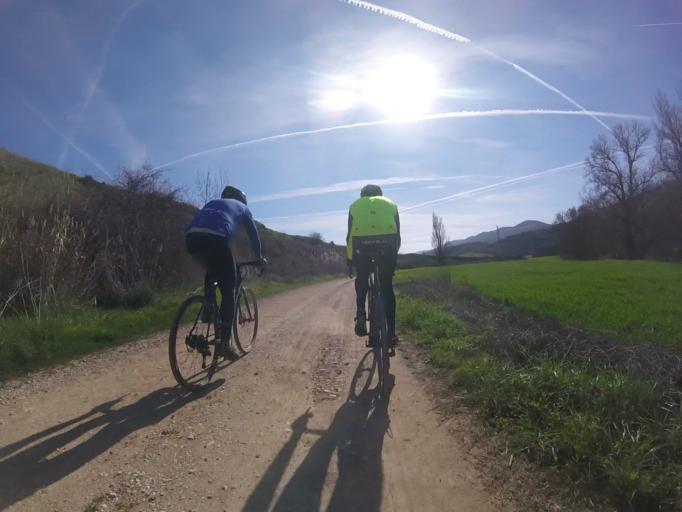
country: ES
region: Navarre
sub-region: Provincia de Navarra
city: Cirauqui
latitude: 42.6710
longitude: -1.9089
